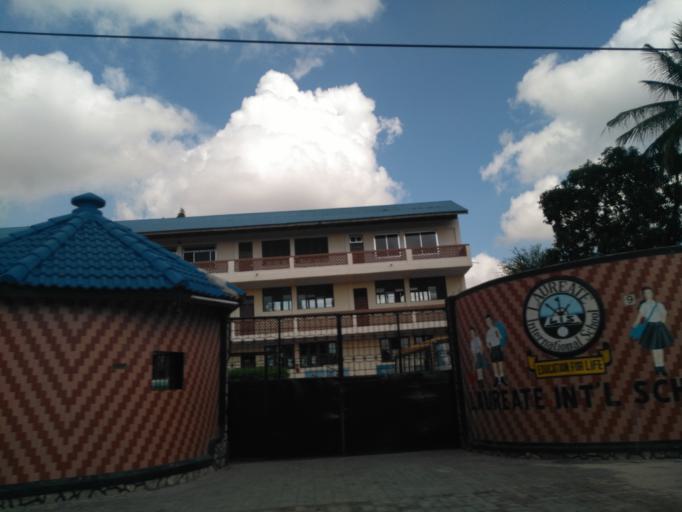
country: TZ
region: Dar es Salaam
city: Magomeni
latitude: -6.7589
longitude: 39.2440
